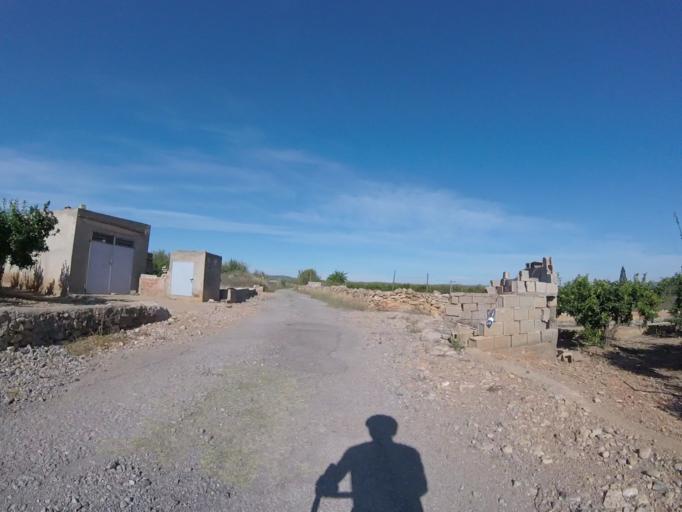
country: ES
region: Valencia
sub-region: Provincia de Castello
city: Torreblanca
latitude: 40.2092
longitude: 0.2340
